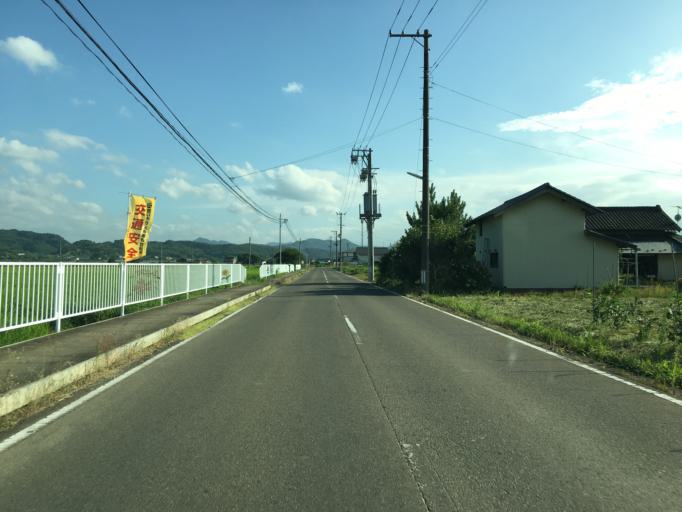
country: JP
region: Fukushima
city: Yanagawamachi-saiwaicho
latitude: 37.8324
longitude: 140.5834
